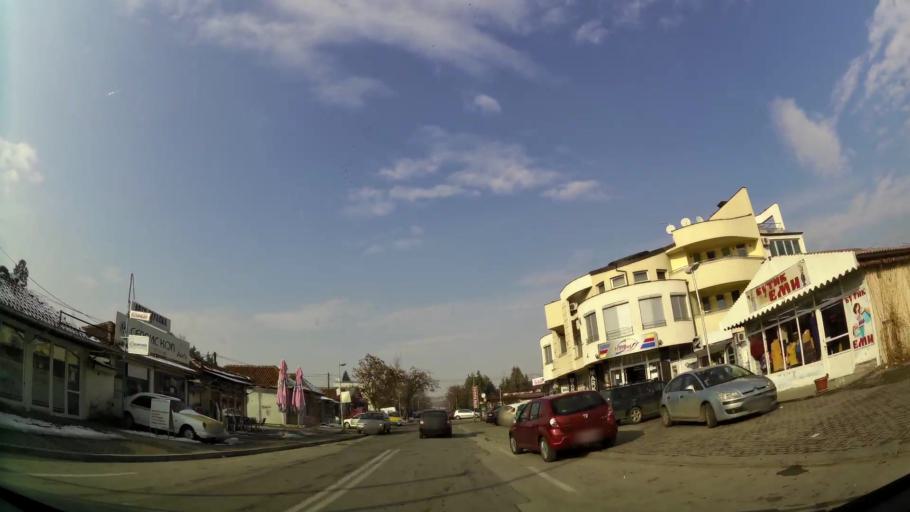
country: MK
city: Creshevo
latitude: 42.0067
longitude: 21.5030
